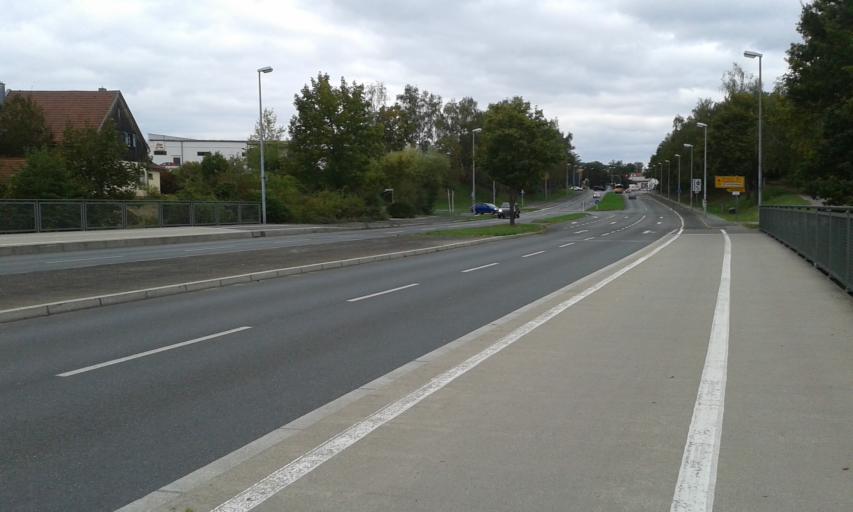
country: DE
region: Bavaria
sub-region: Upper Franconia
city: Bamberg
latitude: 49.8746
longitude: 10.8879
